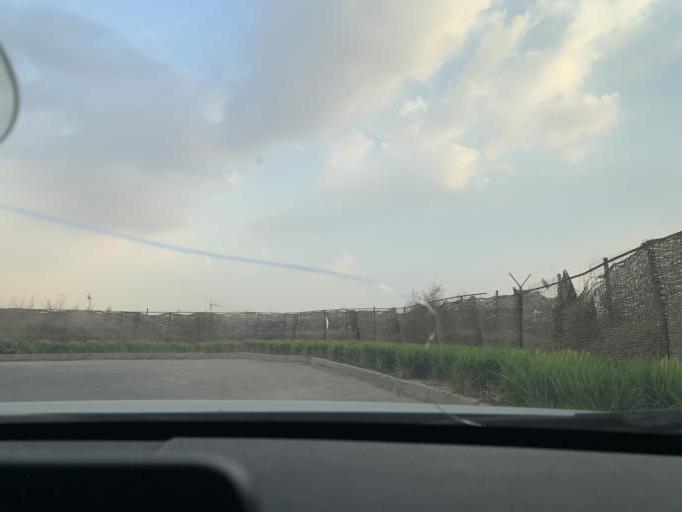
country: EG
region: Muhafazat al Qalyubiyah
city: Al Khankah
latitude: 30.0963
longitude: 31.6576
